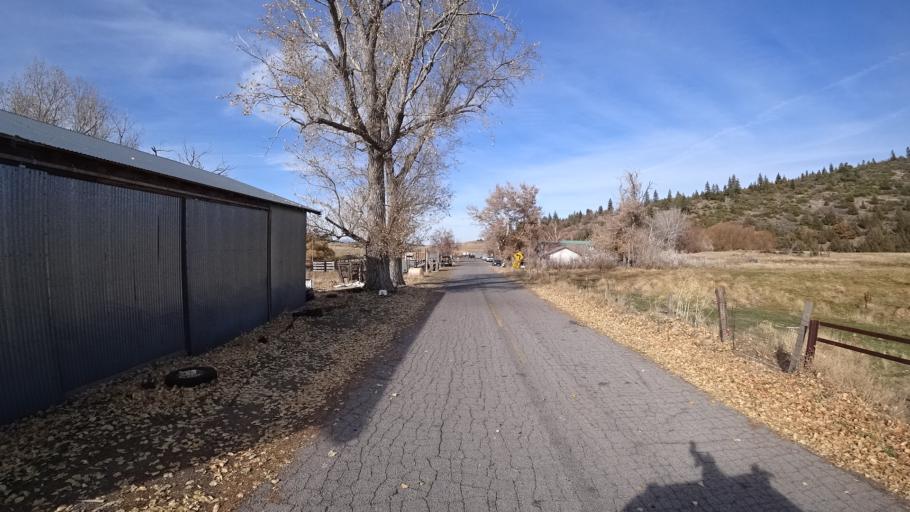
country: US
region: California
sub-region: Siskiyou County
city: Weed
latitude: 41.4638
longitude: -122.3870
